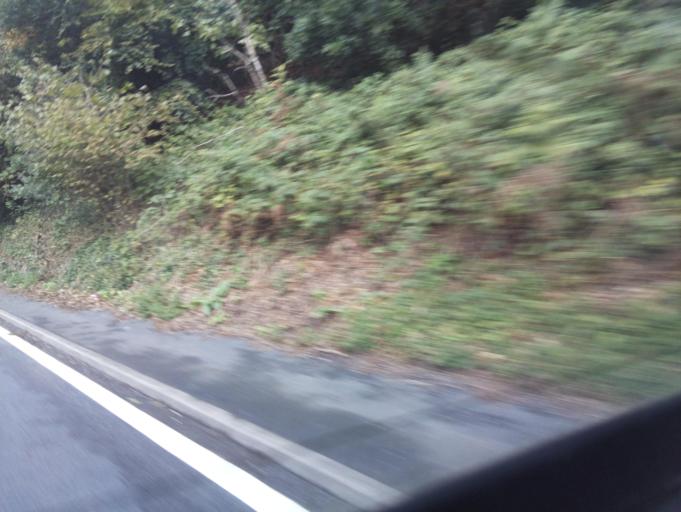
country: GB
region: England
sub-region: Shropshire
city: Bridgnorth
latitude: 52.5422
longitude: -2.4097
